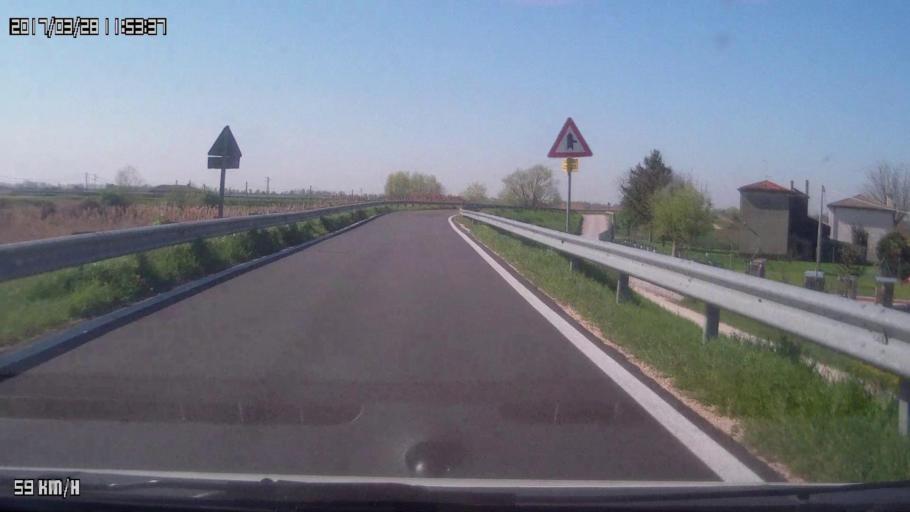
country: IT
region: Veneto
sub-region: Provincia di Venezia
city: Boscochiaro
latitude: 45.1395
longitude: 12.1695
